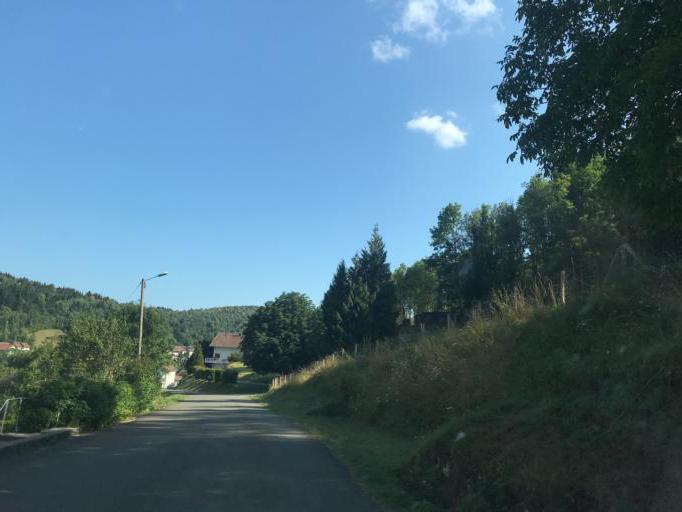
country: FR
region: Franche-Comte
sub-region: Departement du Jura
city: Moirans-en-Montagne
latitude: 46.4109
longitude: 5.7354
